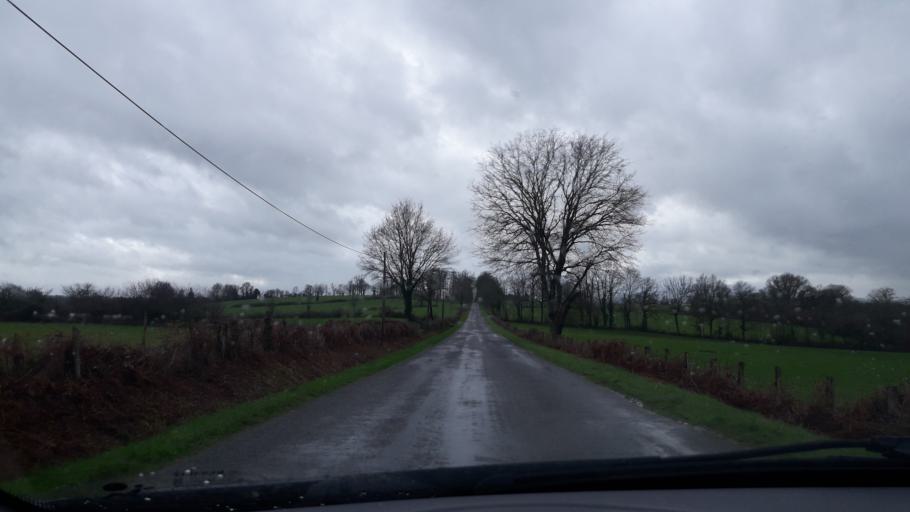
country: FR
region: Limousin
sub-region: Departement de la Haute-Vienne
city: Saint-Paul
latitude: 45.7532
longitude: 1.4162
